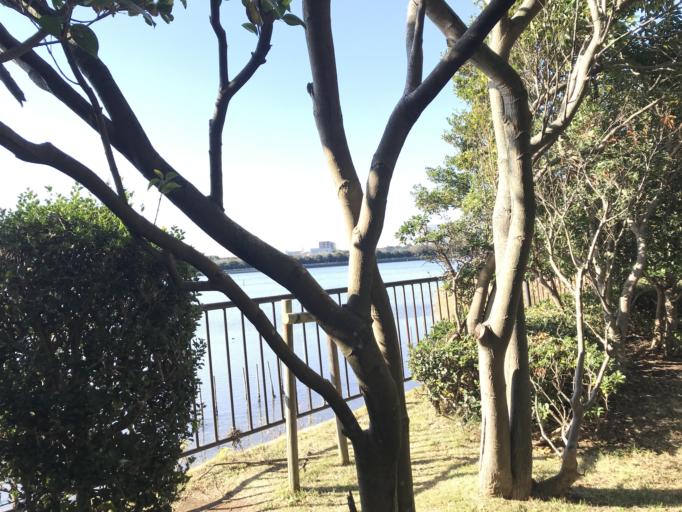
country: JP
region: Chiba
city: Funabashi
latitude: 35.6792
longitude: 140.0072
